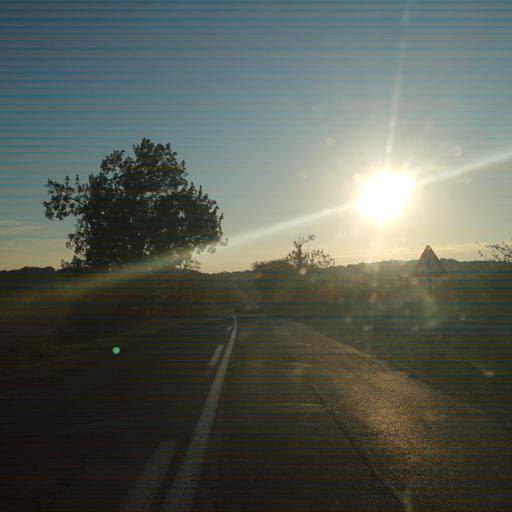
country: RS
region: Central Serbia
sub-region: Borski Okrug
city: Negotin
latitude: 44.2090
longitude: 22.4369
